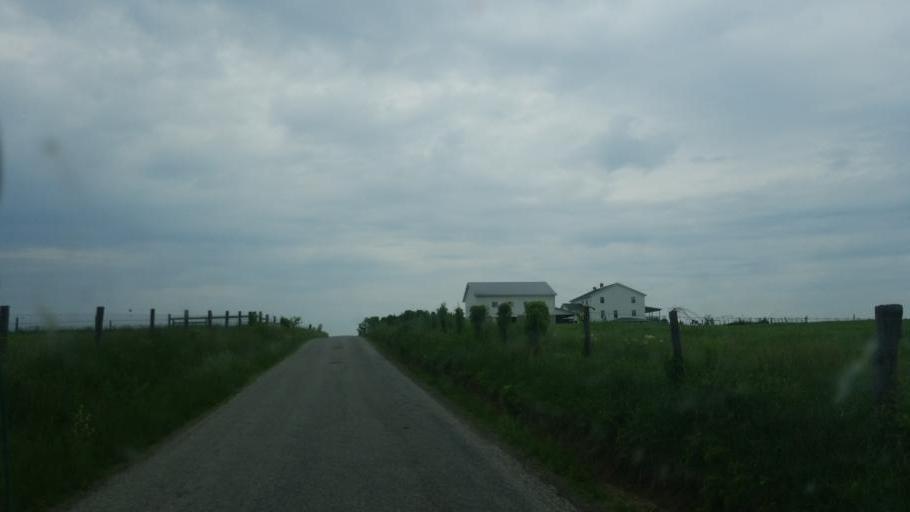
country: US
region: Ohio
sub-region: Wayne County
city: Apple Creek
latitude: 40.6363
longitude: -81.7361
